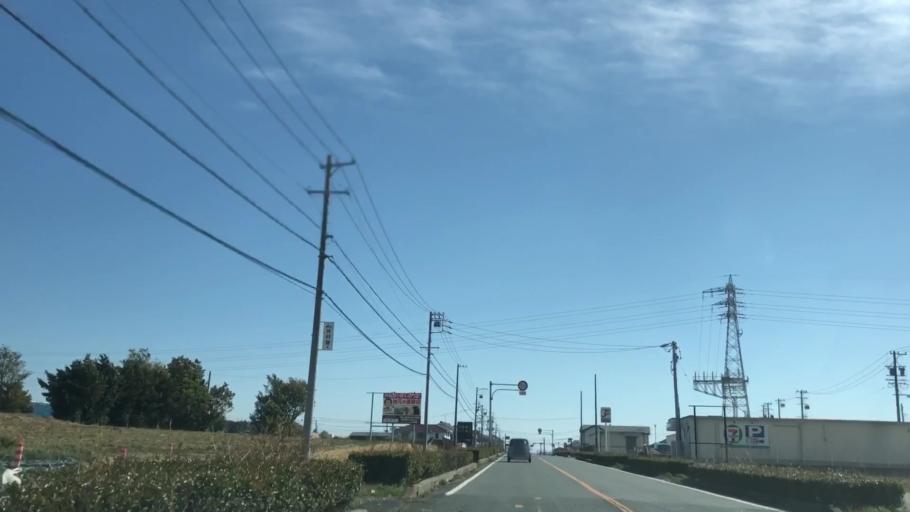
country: JP
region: Aichi
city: Toyohashi
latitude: 34.7093
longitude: 137.4096
